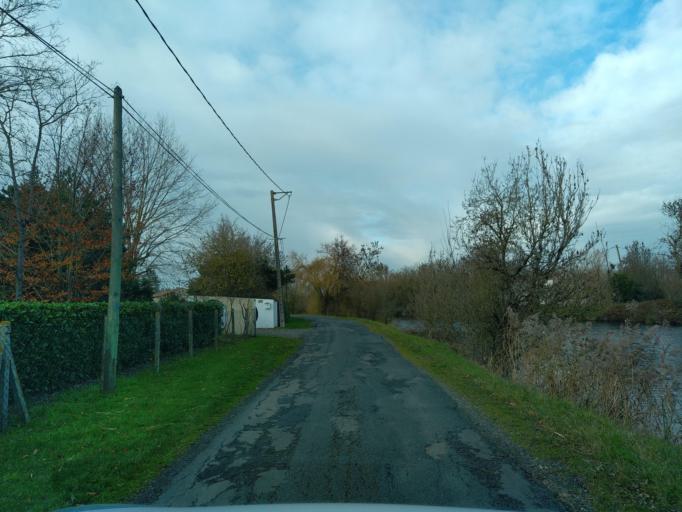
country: FR
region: Pays de la Loire
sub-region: Departement de la Vendee
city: Vix
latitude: 46.3331
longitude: -0.8081
